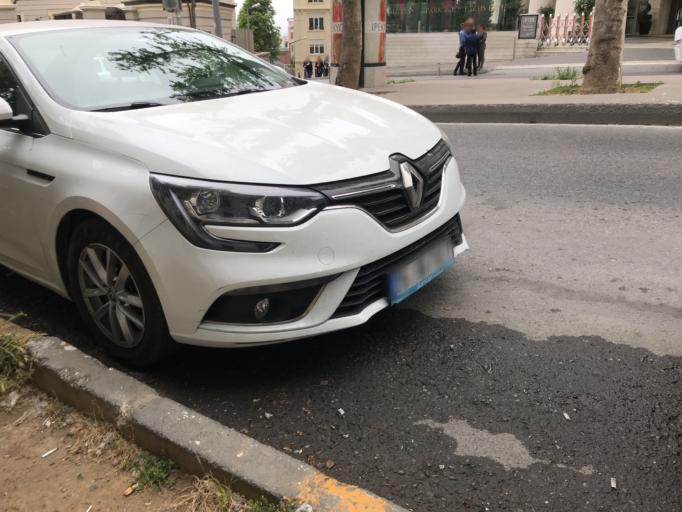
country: TR
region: Istanbul
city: Eminoenue
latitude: 41.0355
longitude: 28.9884
